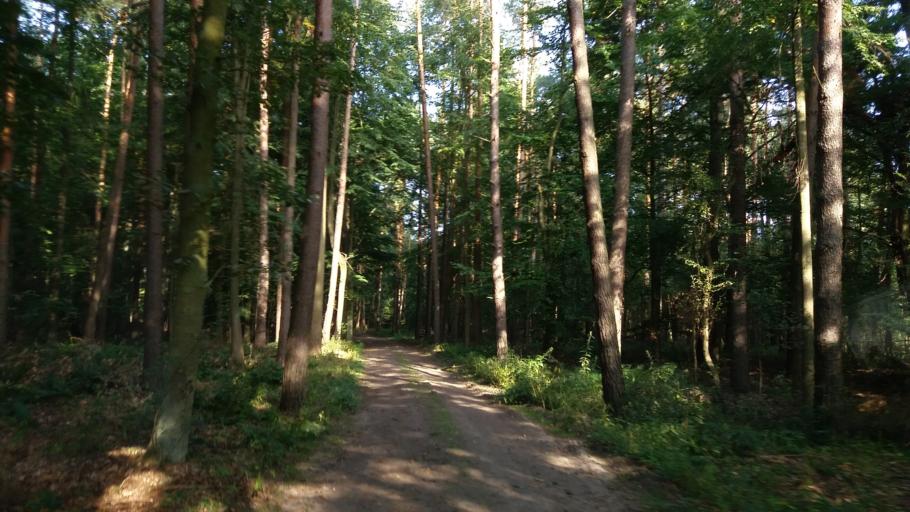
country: PL
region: West Pomeranian Voivodeship
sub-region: Powiat choszczenski
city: Choszczno
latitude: 53.2285
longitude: 15.4488
